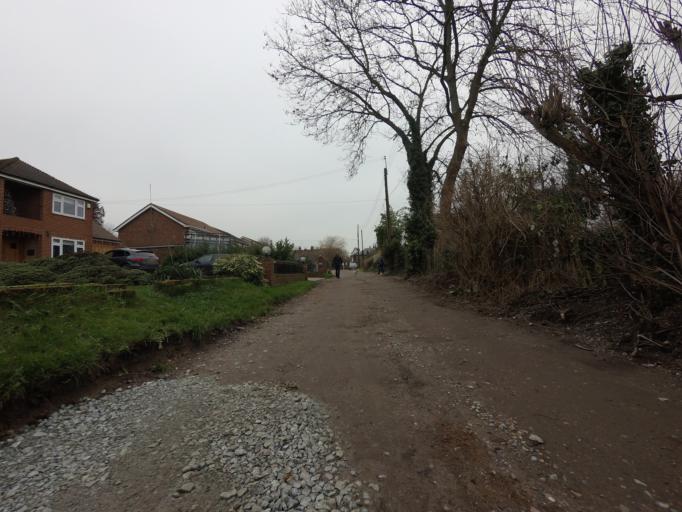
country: GB
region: England
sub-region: Kent
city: Eynsford
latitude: 51.3801
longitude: 0.2246
